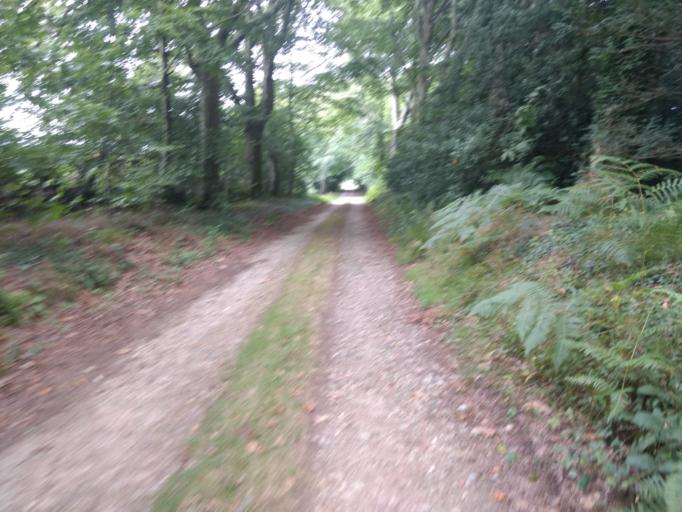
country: FR
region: Brittany
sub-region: Departement du Finistere
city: Loperhet
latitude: 48.3713
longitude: -4.2933
